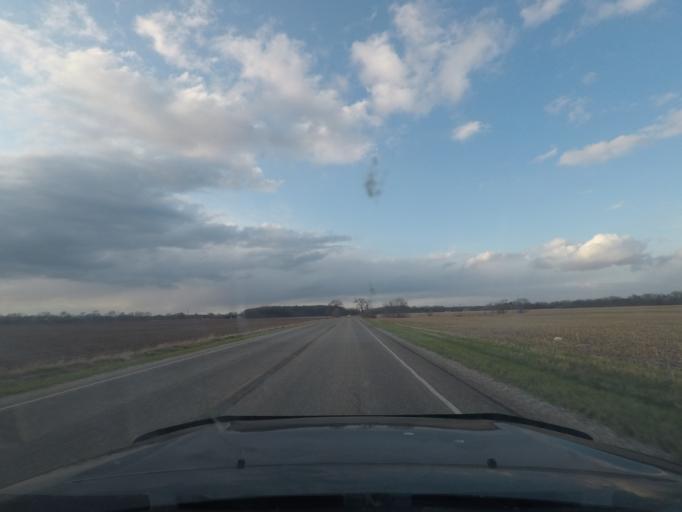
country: US
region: Indiana
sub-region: LaPorte County
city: Kingsford Heights
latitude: 41.5364
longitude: -86.7406
